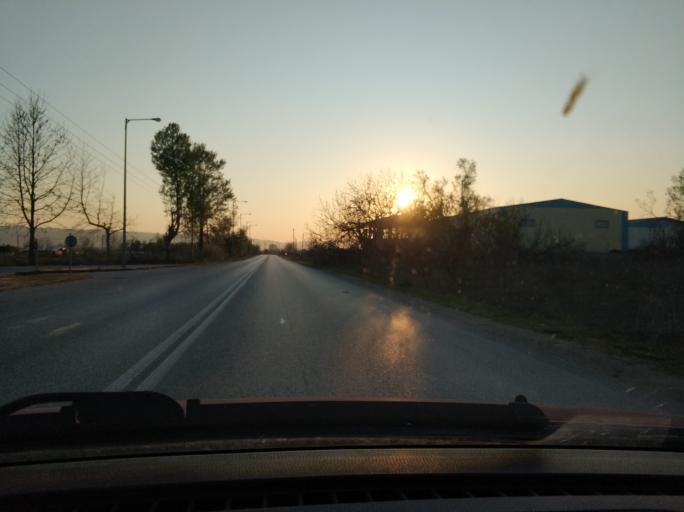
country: GR
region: Central Macedonia
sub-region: Nomos Thessalonikis
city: Lagkadas
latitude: 40.7494
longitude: 23.1002
